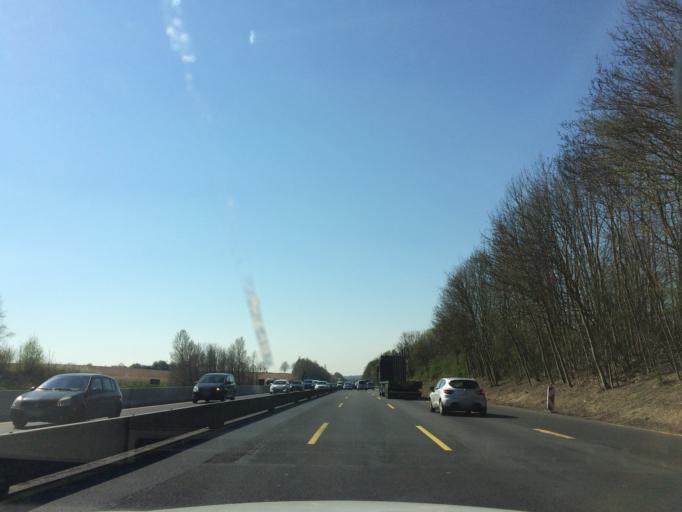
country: DE
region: North Rhine-Westphalia
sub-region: Regierungsbezirk Dusseldorf
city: Erkrath
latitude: 51.2568
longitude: 6.9140
